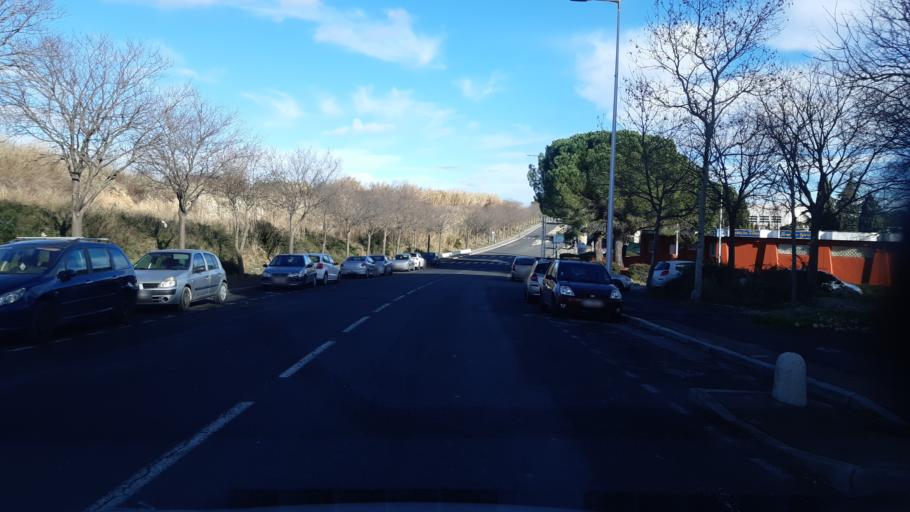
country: FR
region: Languedoc-Roussillon
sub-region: Departement de l'Herault
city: Grabels
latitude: 43.6416
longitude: 3.8126
